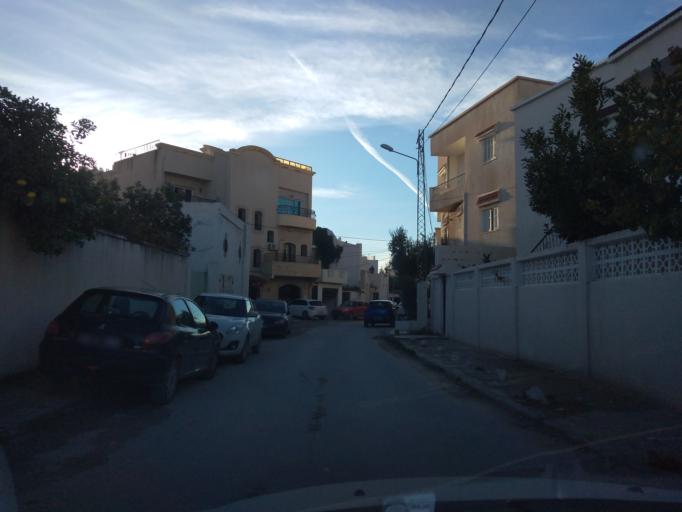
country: TN
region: Manouba
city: Manouba
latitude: 36.8193
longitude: 10.1268
